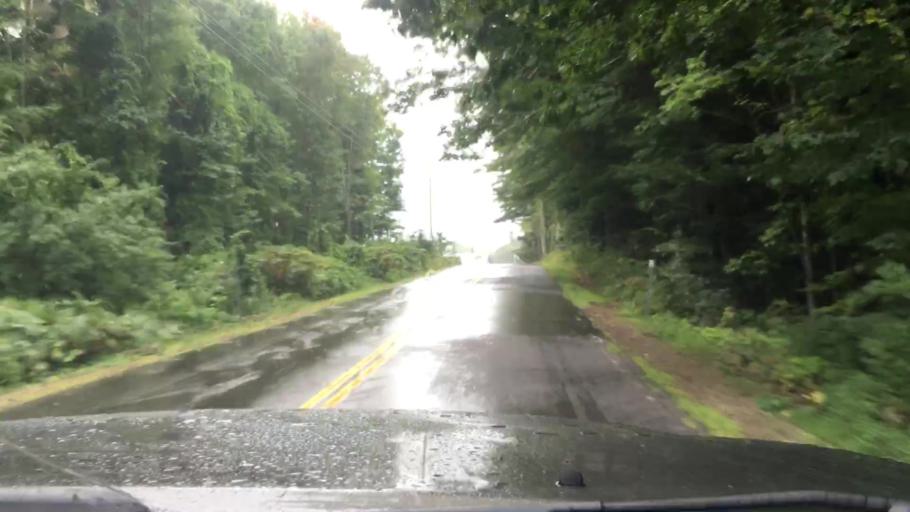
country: US
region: New Hampshire
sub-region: Belknap County
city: Meredith
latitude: 43.6744
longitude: -71.5270
